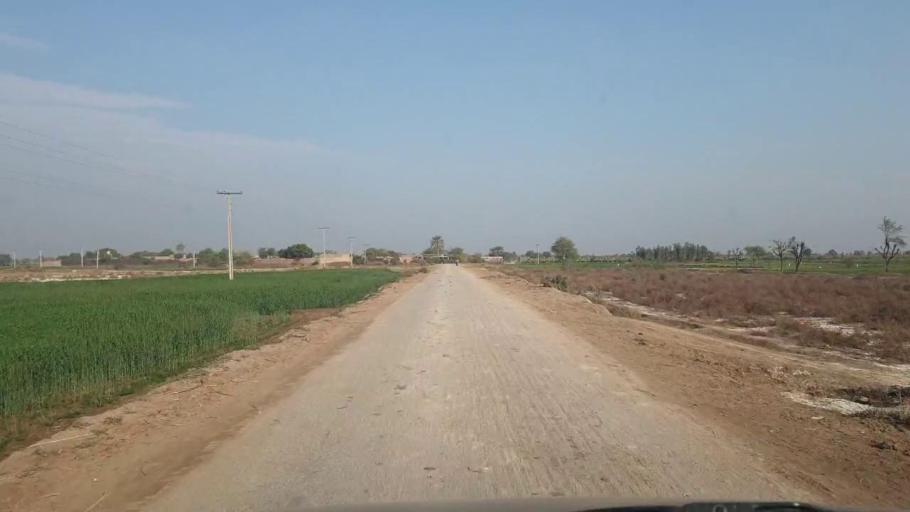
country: PK
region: Sindh
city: Tando Adam
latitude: 25.7440
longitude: 68.6070
